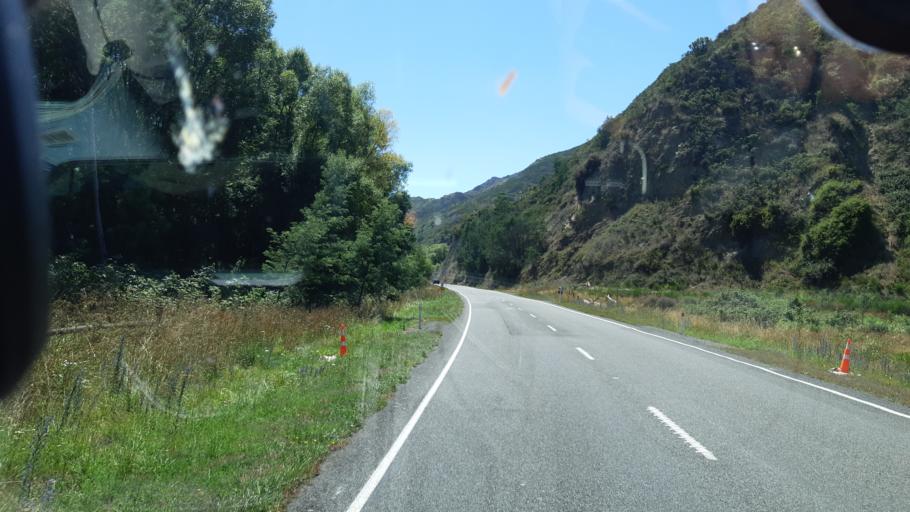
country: NZ
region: Canterbury
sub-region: Kaikoura District
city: Kaikoura
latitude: -42.6365
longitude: 173.3442
